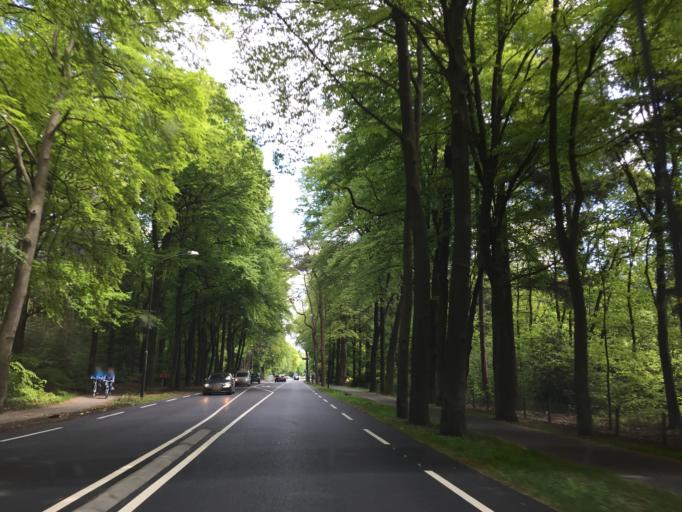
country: NL
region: Gelderland
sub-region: Gemeente Apeldoorn
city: Apeldoorn
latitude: 52.2269
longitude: 5.9402
